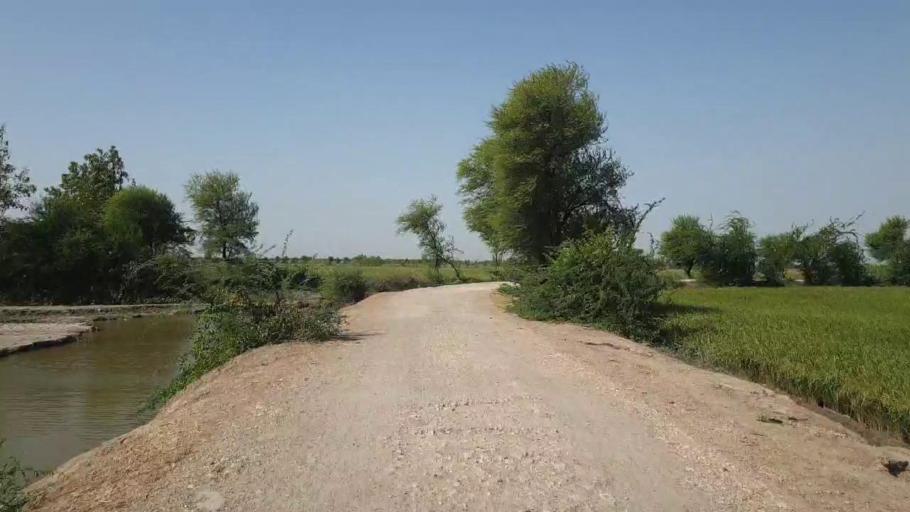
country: PK
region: Sindh
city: Tando Bago
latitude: 24.7566
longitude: 69.0254
